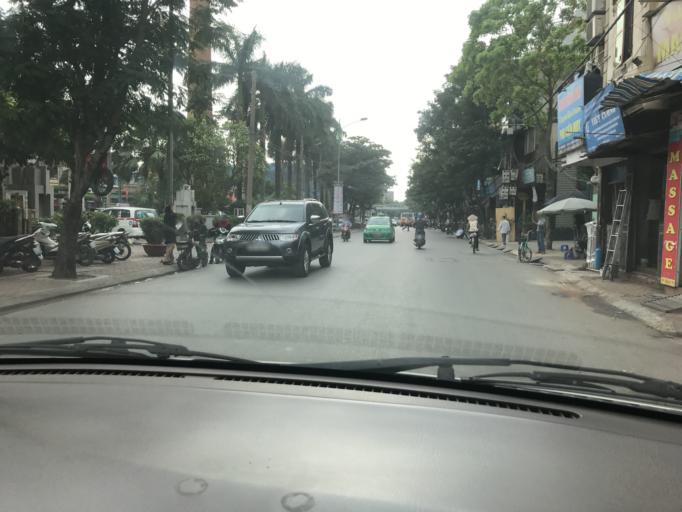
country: VN
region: Ha Noi
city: Dong Da
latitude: 21.0304
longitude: 105.8285
